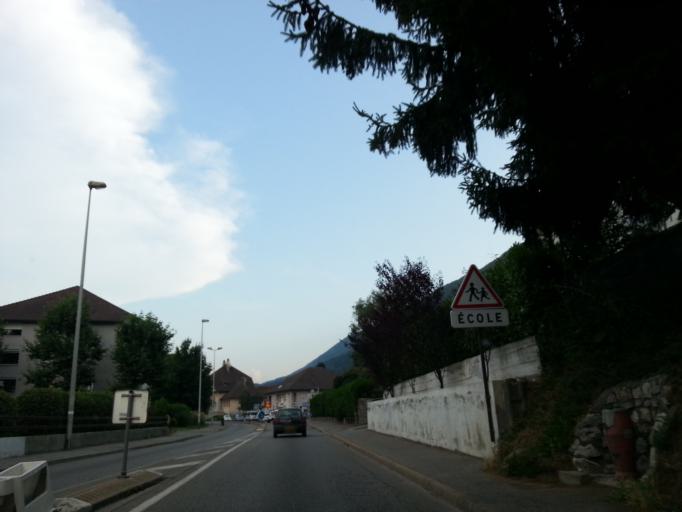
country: FR
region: Rhone-Alpes
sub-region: Departement de la Haute-Savoie
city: Sevrier
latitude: 45.8665
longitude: 6.1399
